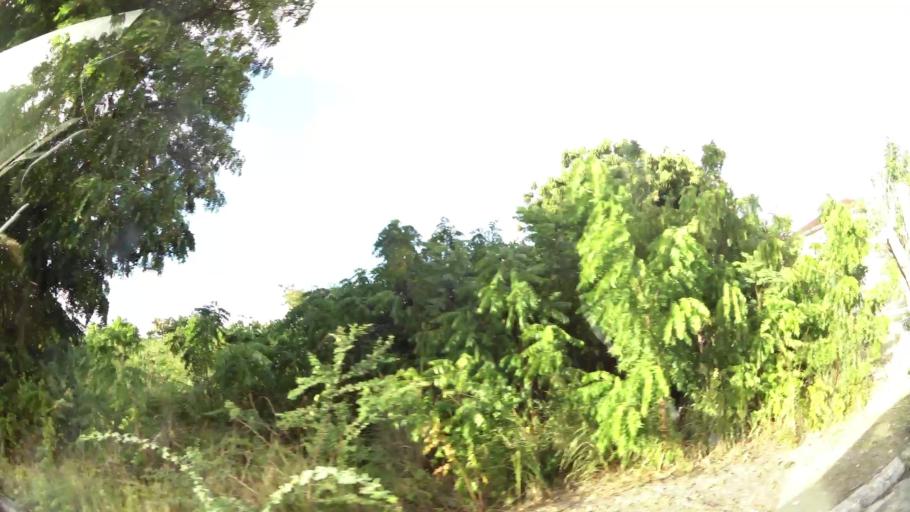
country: AG
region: Saint George
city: Piggotts
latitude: 17.1646
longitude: -61.8153
